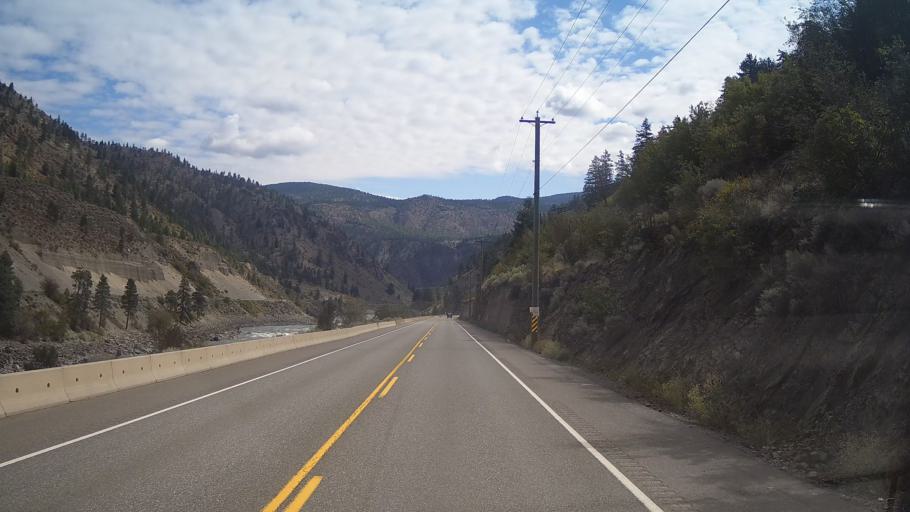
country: CA
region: British Columbia
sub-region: Thompson-Nicola Regional District
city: Ashcroft
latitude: 50.2590
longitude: -121.4297
